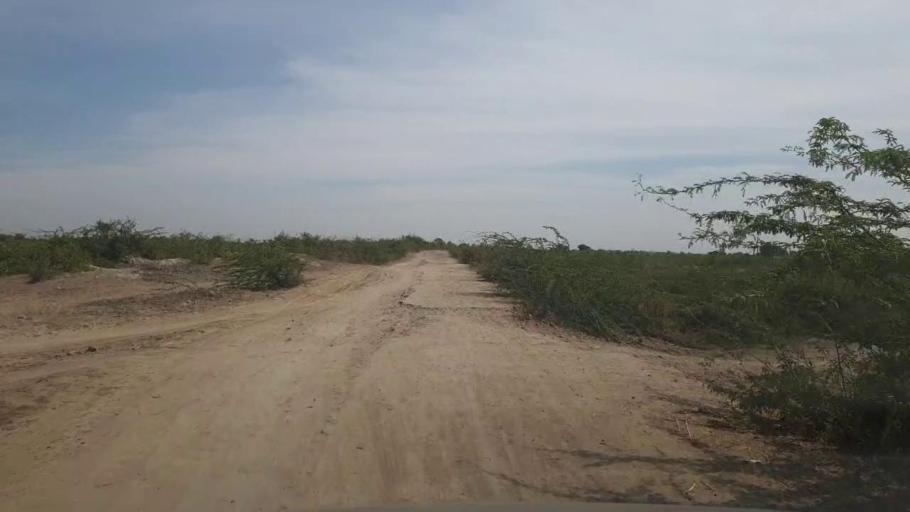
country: PK
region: Sindh
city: Kunri
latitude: 25.2904
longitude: 69.5875
